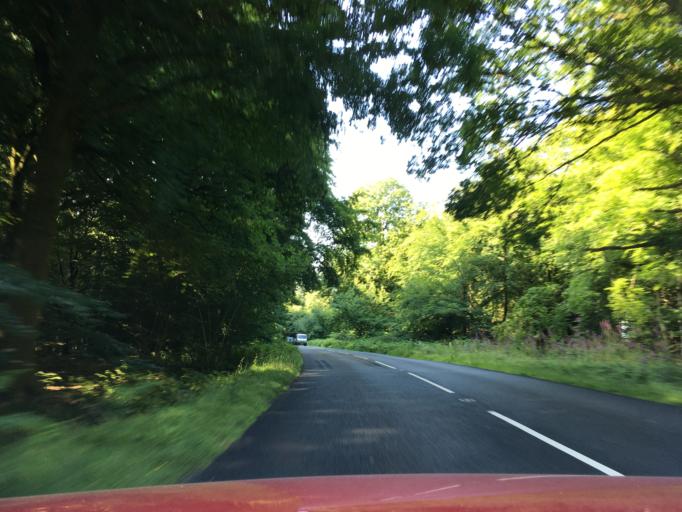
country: GB
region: England
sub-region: Gloucestershire
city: Lydbrook
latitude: 51.7999
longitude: -2.5508
